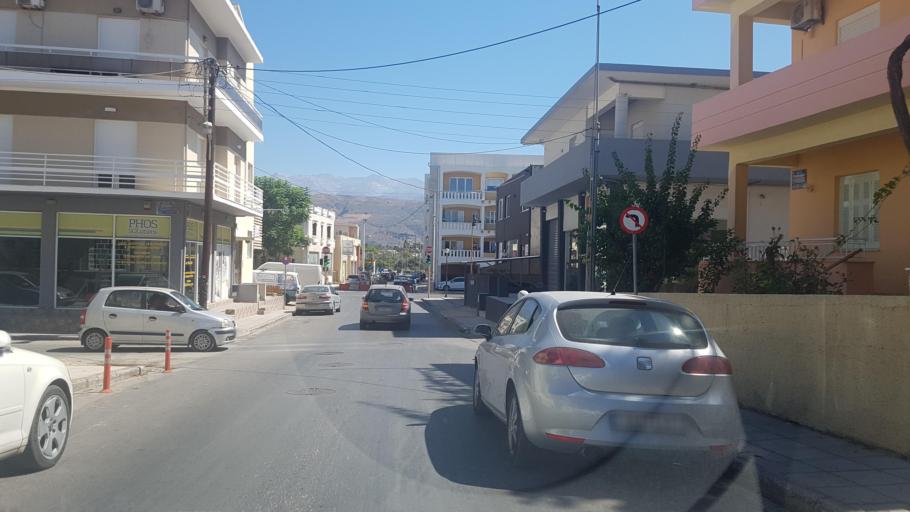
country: GR
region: Crete
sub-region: Nomos Chanias
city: Chania
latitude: 35.5048
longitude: 24.0178
